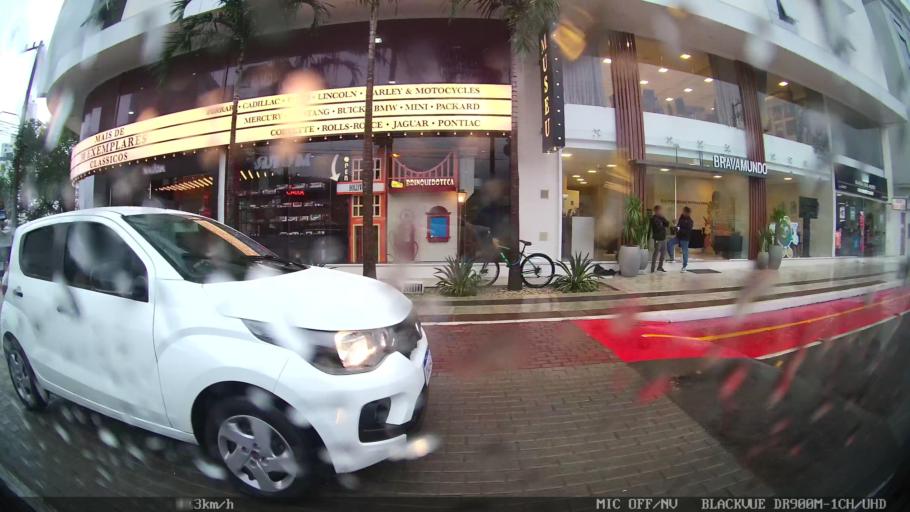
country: BR
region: Santa Catarina
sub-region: Balneario Camboriu
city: Balneario Camboriu
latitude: -27.0064
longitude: -48.6044
